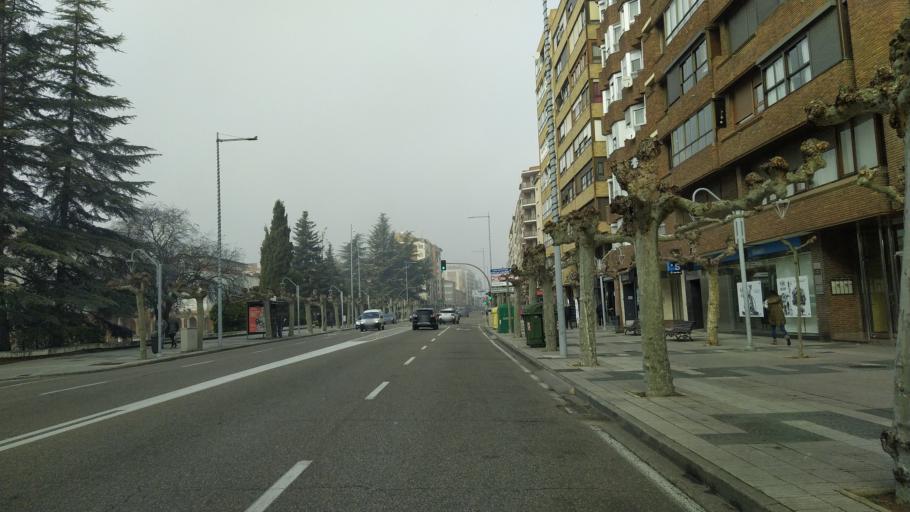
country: ES
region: Castille and Leon
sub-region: Provincia de Palencia
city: Palencia
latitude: 42.0006
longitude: -4.5261
